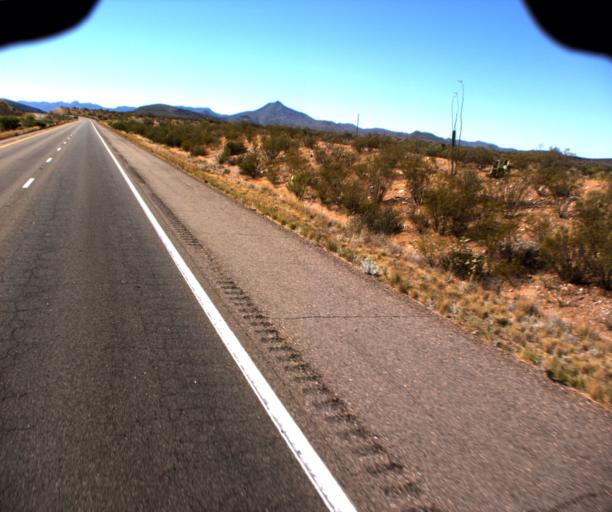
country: US
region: Arizona
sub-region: Yavapai County
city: Bagdad
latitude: 34.6011
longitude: -113.5196
